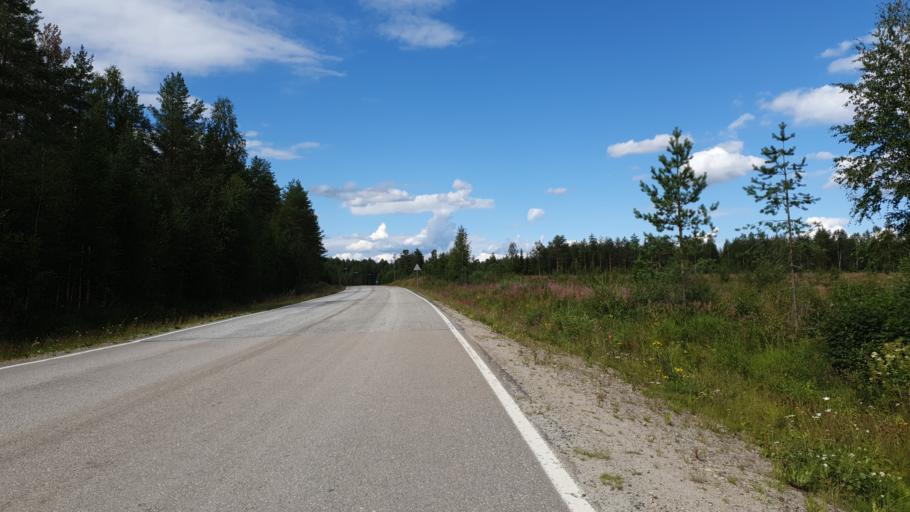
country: FI
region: Kainuu
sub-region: Kehys-Kainuu
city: Kuhmo
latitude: 64.1139
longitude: 29.5277
